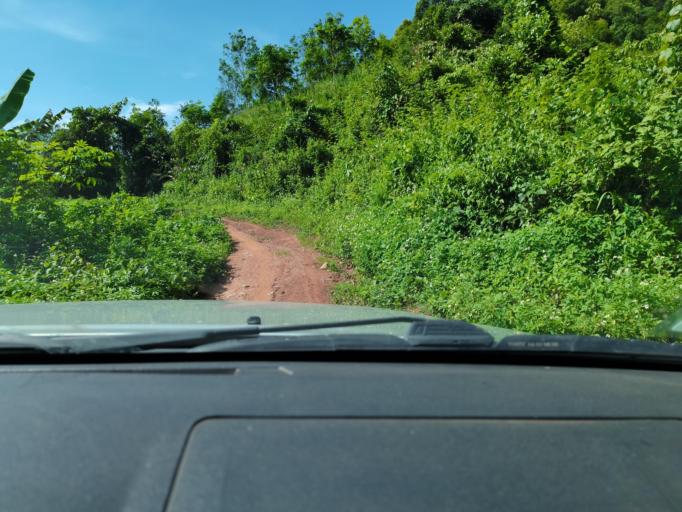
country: LA
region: Loungnamtha
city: Muang Nale
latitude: 20.5499
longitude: 101.0659
